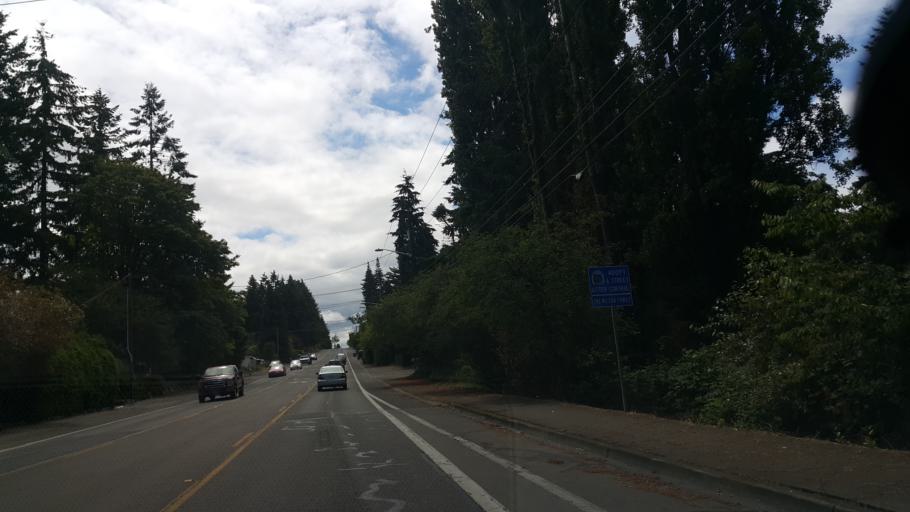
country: US
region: Washington
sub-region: Pierce County
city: Fircrest
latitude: 47.2274
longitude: -122.5264
